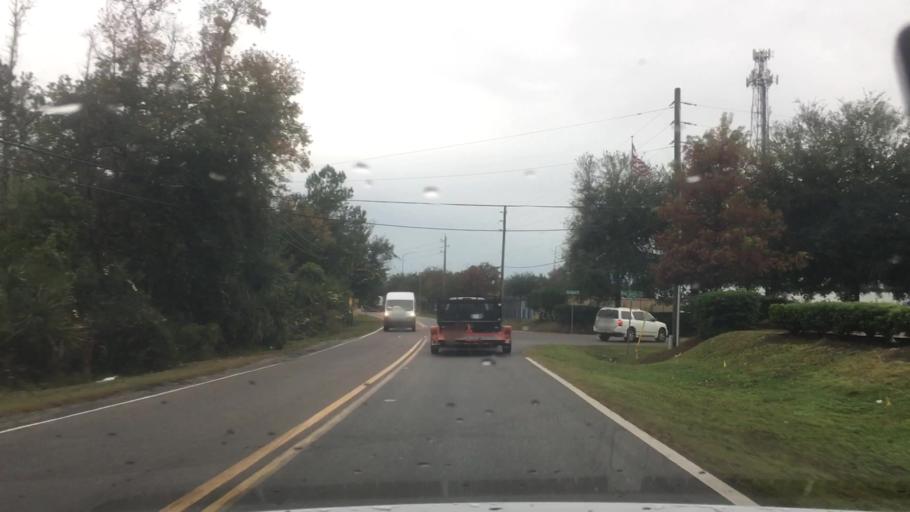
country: US
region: Florida
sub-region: Duval County
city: Jacksonville
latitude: 30.4218
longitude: -81.5649
